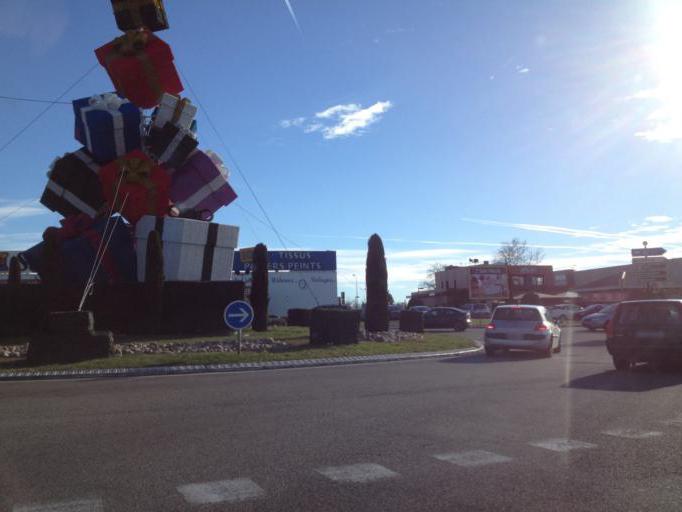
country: FR
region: Provence-Alpes-Cote d'Azur
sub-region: Departement du Vaucluse
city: Vedene
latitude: 43.9799
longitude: 4.8787
